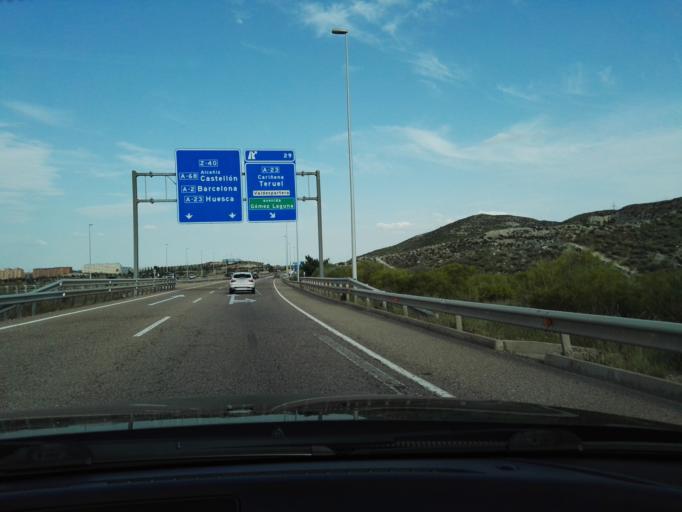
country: ES
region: Aragon
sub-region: Provincia de Zaragoza
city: Montecanal
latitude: 41.6179
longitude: -0.9406
